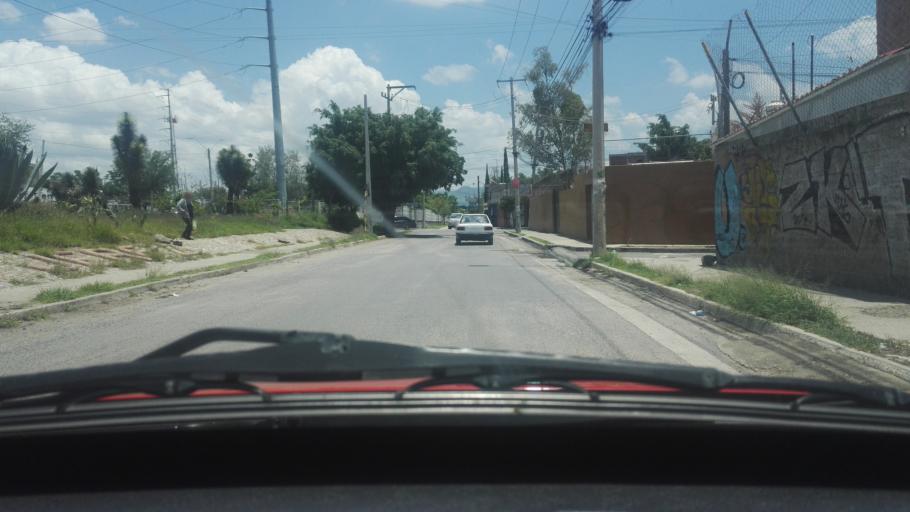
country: MX
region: Guanajuato
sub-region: Leon
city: Fraccionamiento Paraiso Real
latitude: 21.0897
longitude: -101.6282
